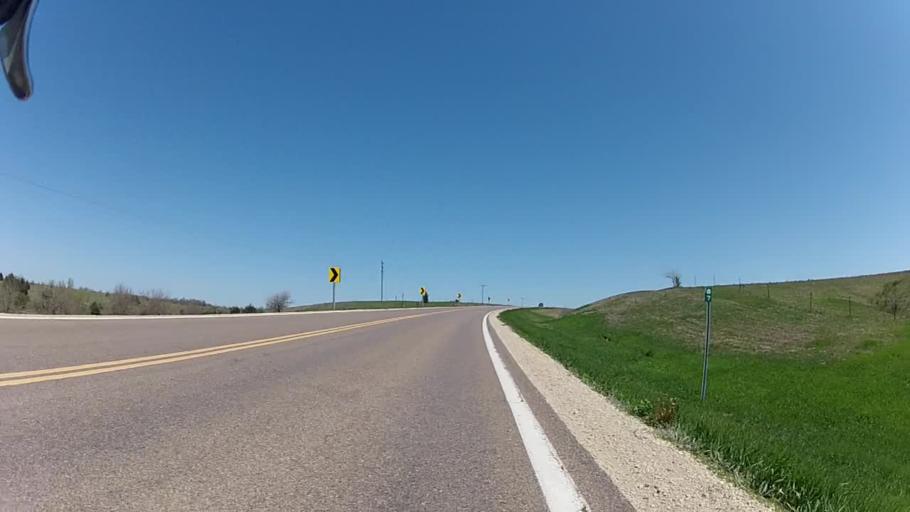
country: US
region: Kansas
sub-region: Wabaunsee County
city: Alma
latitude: 38.9293
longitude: -96.5207
